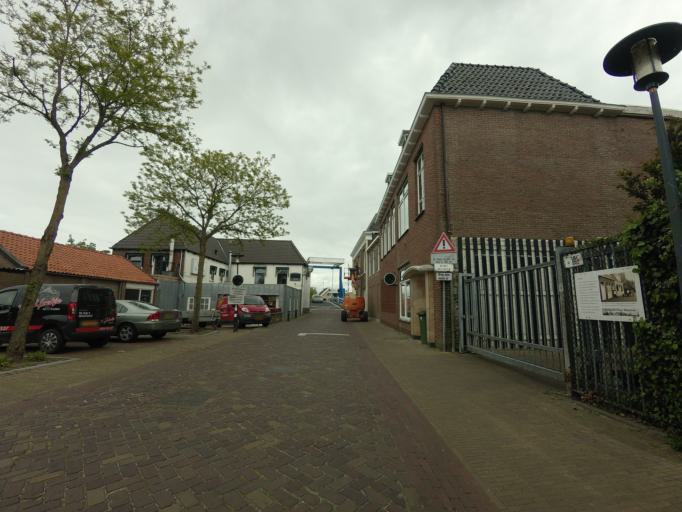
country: NL
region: Friesland
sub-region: Sudwest Fryslan
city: Woudsend
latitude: 52.9436
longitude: 5.6296
